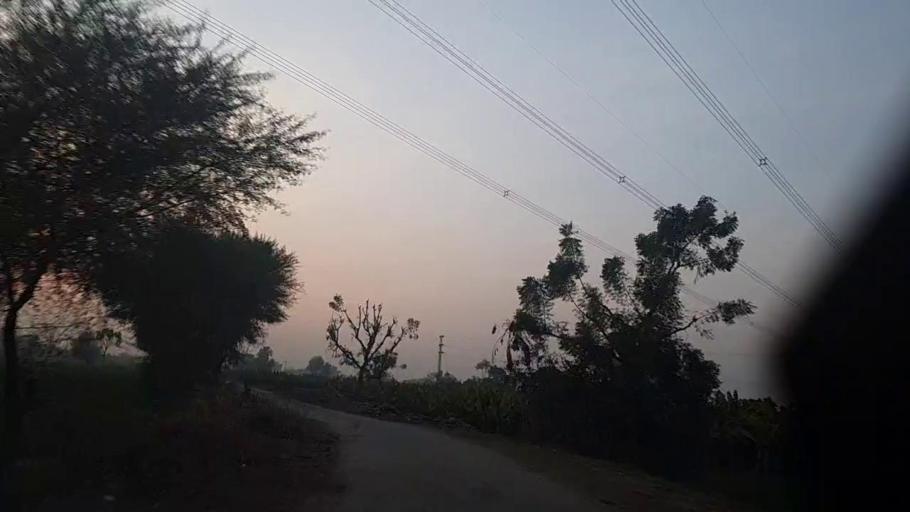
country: PK
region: Sindh
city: Sakrand
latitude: 26.1006
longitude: 68.3228
